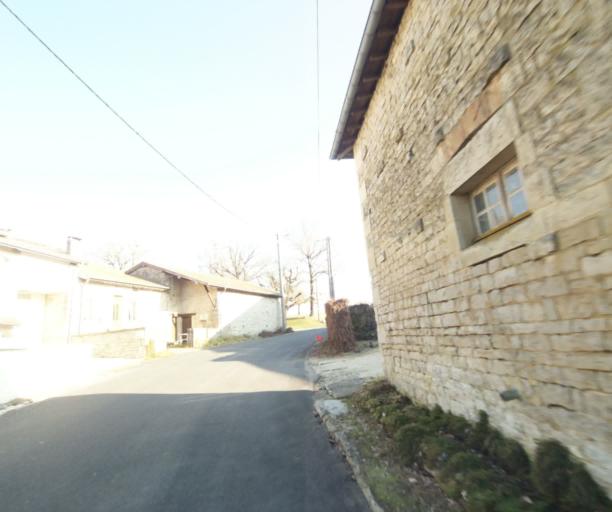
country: FR
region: Champagne-Ardenne
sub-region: Departement de la Haute-Marne
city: Chevillon
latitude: 48.4924
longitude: 5.0703
